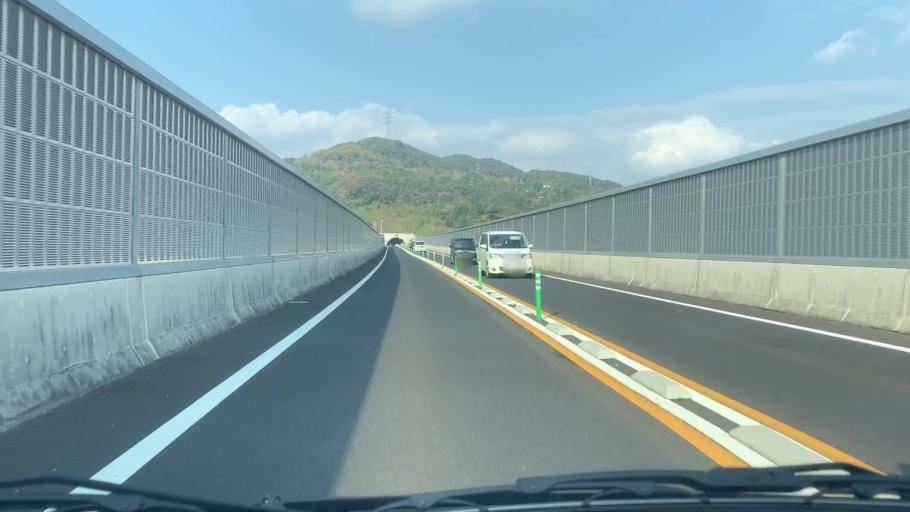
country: JP
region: Nagasaki
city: Sasebo
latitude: 33.0828
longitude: 129.7764
